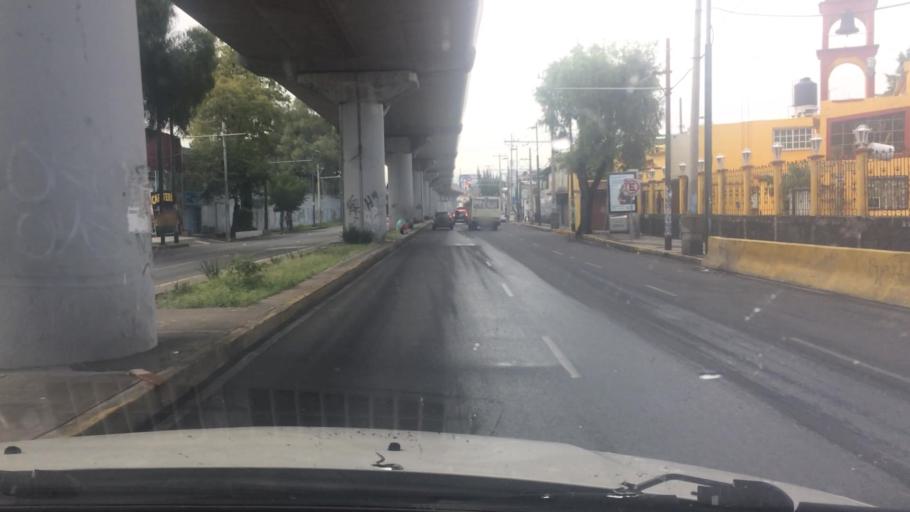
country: MX
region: Mexico City
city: Iztapalapa
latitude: 19.3340
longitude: -99.1087
